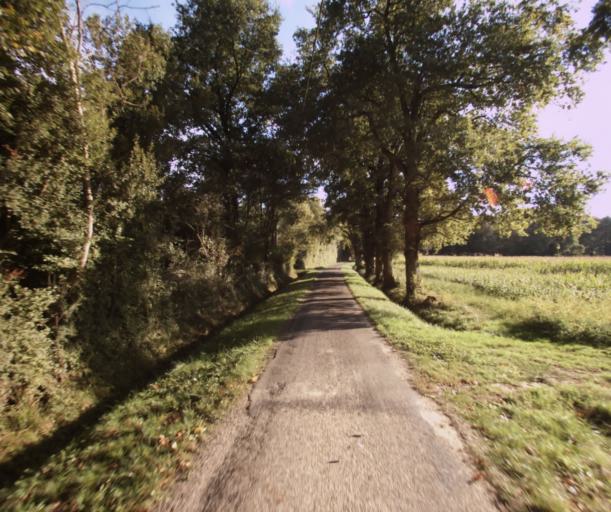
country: FR
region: Midi-Pyrenees
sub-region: Departement du Gers
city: Eauze
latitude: 43.8545
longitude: 0.0324
